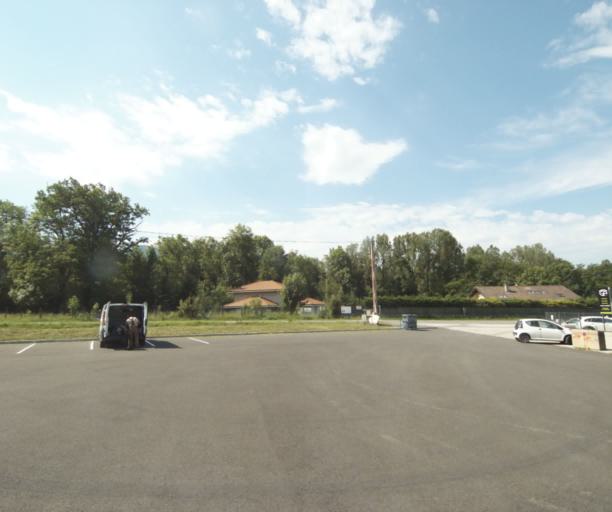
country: FR
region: Rhone-Alpes
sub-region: Departement de la Haute-Savoie
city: Allinges
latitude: 46.3348
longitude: 6.4891
